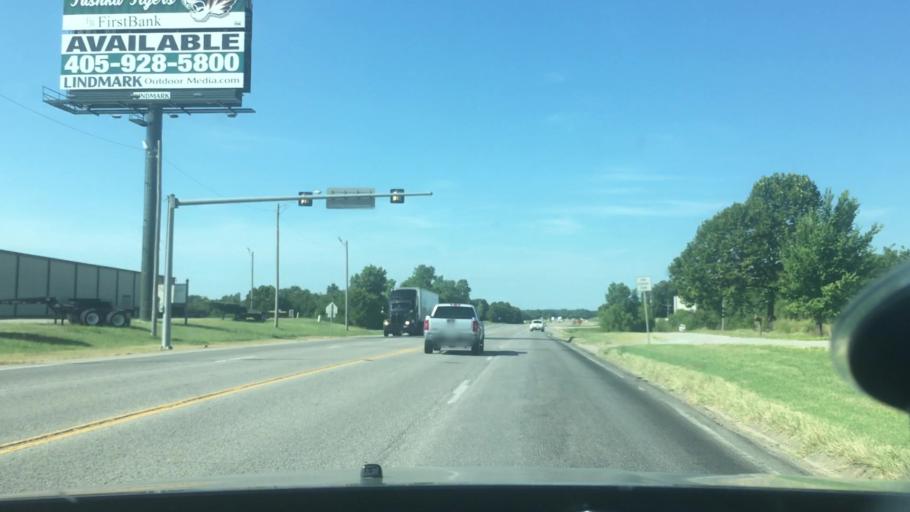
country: US
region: Oklahoma
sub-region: Atoka County
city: Atoka
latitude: 34.3159
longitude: -96.1700
